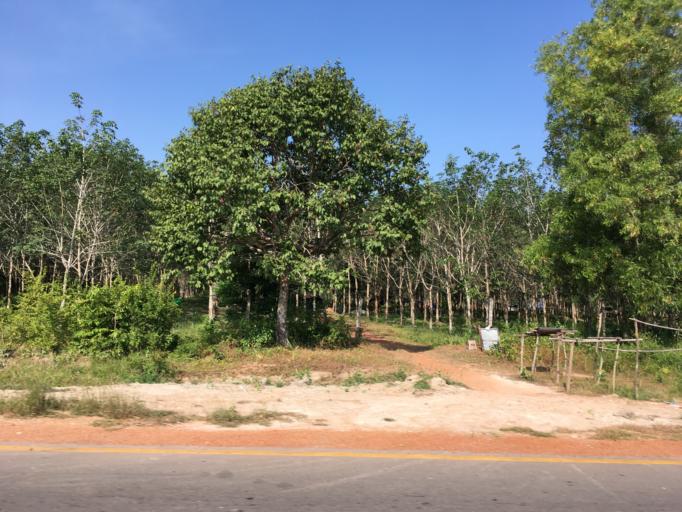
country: MM
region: Mon
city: Martaban
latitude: 16.6543
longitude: 97.7415
